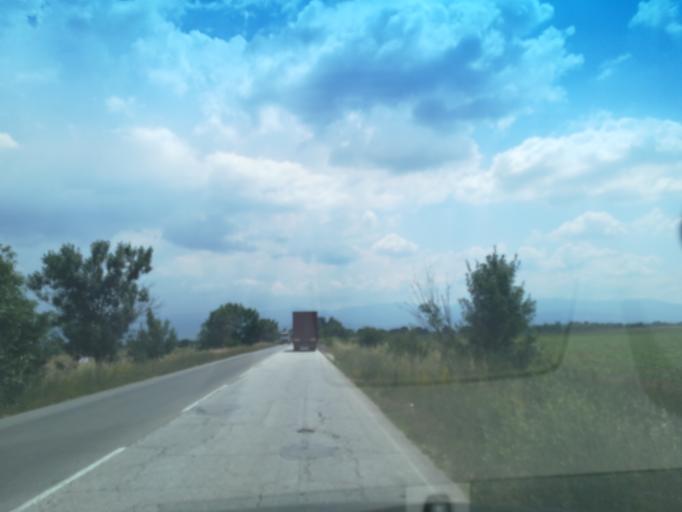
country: BG
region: Plovdiv
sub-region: Obshtina Plovdiv
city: Plovdiv
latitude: 42.1841
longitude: 24.6765
